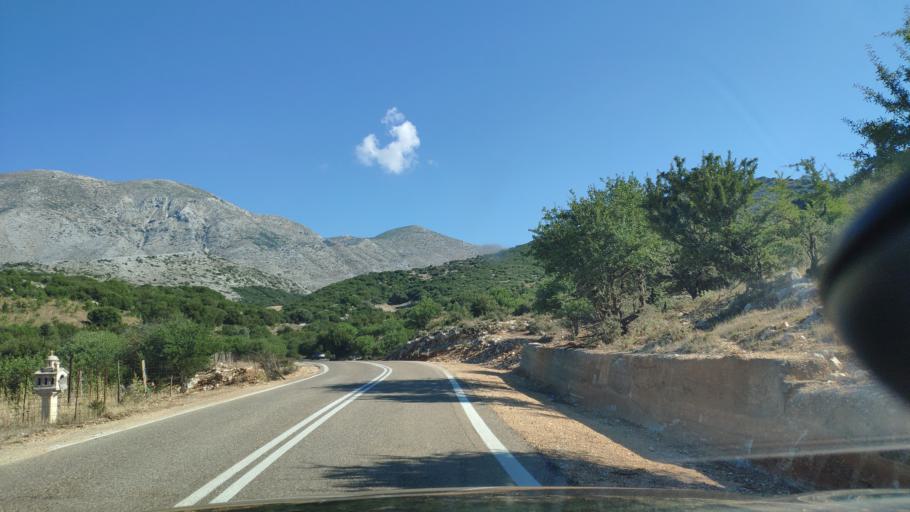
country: GR
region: West Greece
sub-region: Nomos Aitolias kai Akarnanias
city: Archontochorion
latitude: 38.6927
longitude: 21.0599
